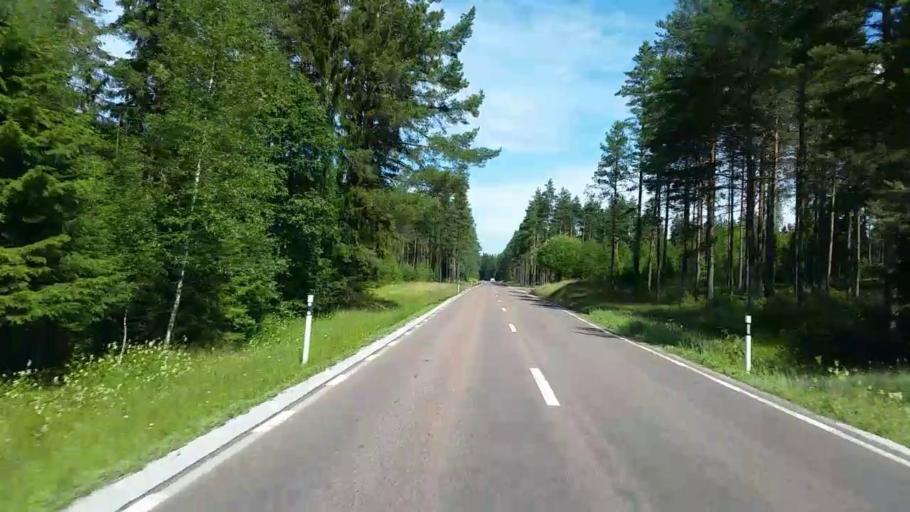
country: SE
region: Dalarna
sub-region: Rattviks Kommun
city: Raettvik
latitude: 60.9065
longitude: 15.1933
